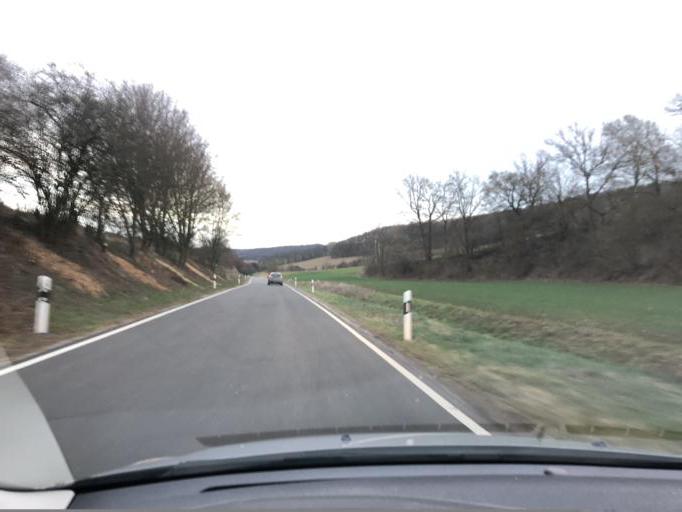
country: DE
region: Saxony-Anhalt
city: Balgstadt
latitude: 51.2060
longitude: 11.7082
